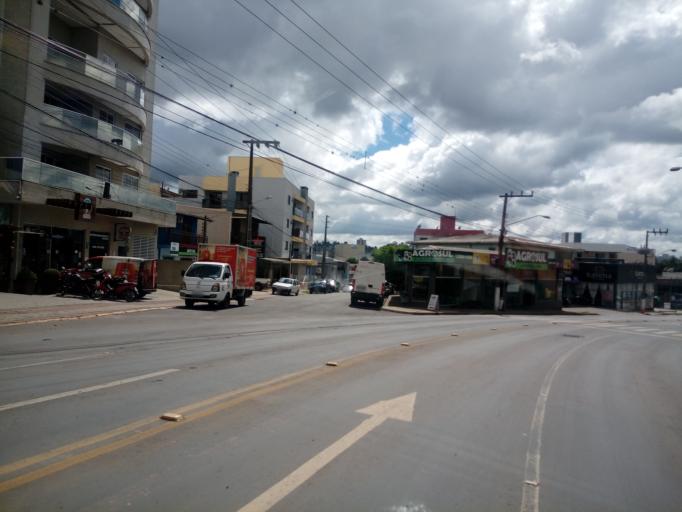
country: BR
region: Santa Catarina
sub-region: Chapeco
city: Chapeco
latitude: -27.0939
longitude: -52.6256
